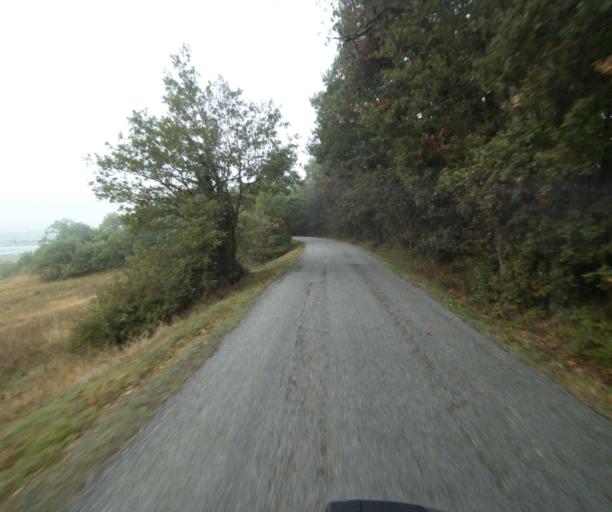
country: FR
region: Midi-Pyrenees
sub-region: Departement du Tarn-et-Garonne
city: Orgueil
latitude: 43.9299
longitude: 1.4296
